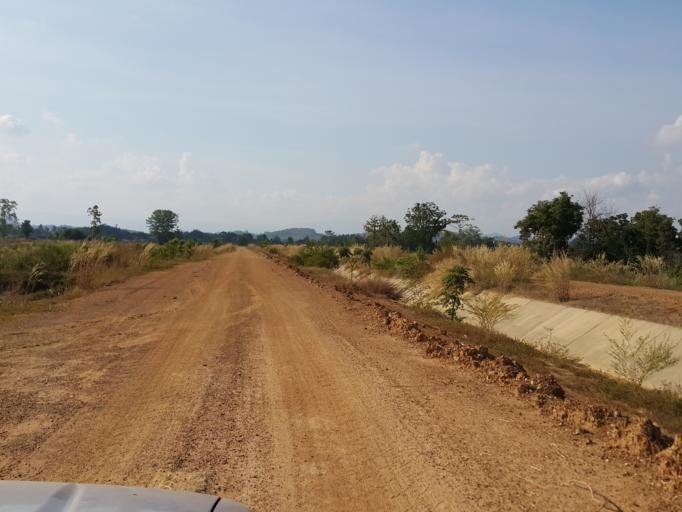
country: TH
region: Sukhothai
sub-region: Amphoe Si Satchanalai
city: Si Satchanalai
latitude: 17.4788
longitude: 99.6573
